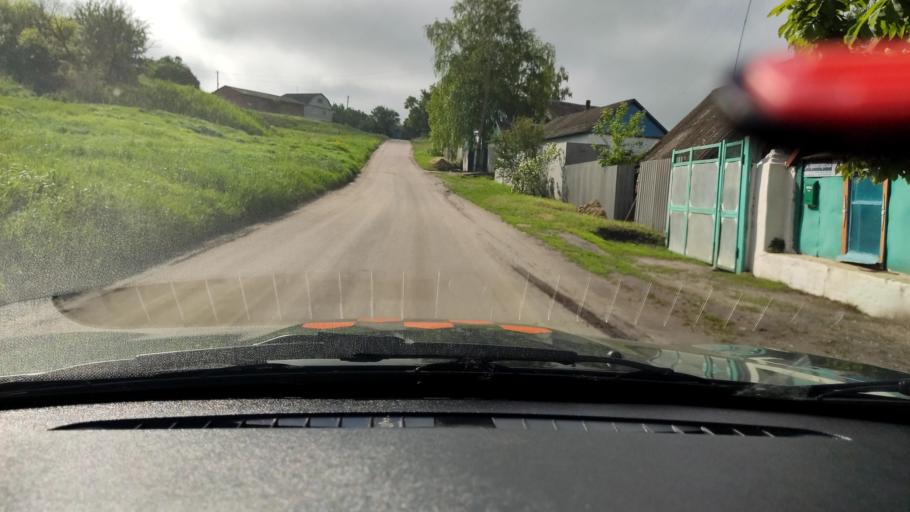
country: RU
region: Voronezj
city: Uryv-Pokrovka
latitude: 51.1103
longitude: 39.1638
